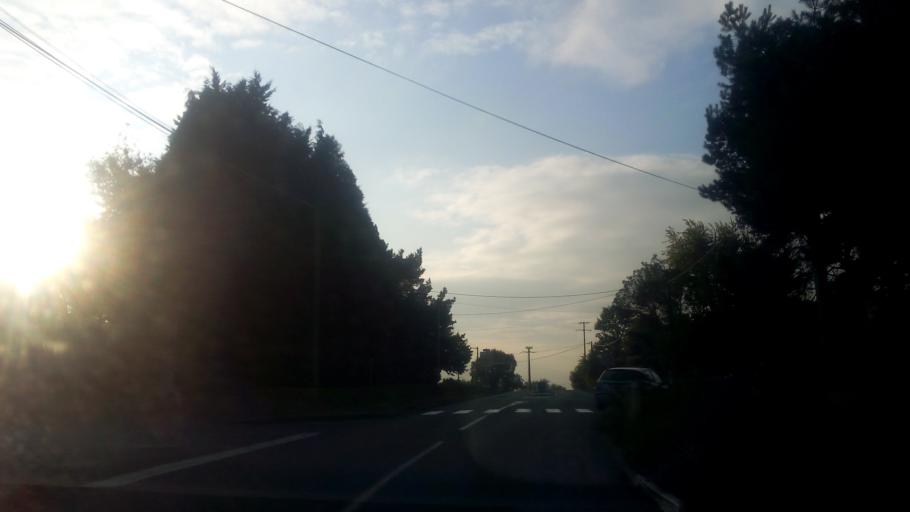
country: FR
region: Brittany
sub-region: Departement du Morbihan
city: Saint-Jean-la-Poterie
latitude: 47.6366
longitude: -2.1313
